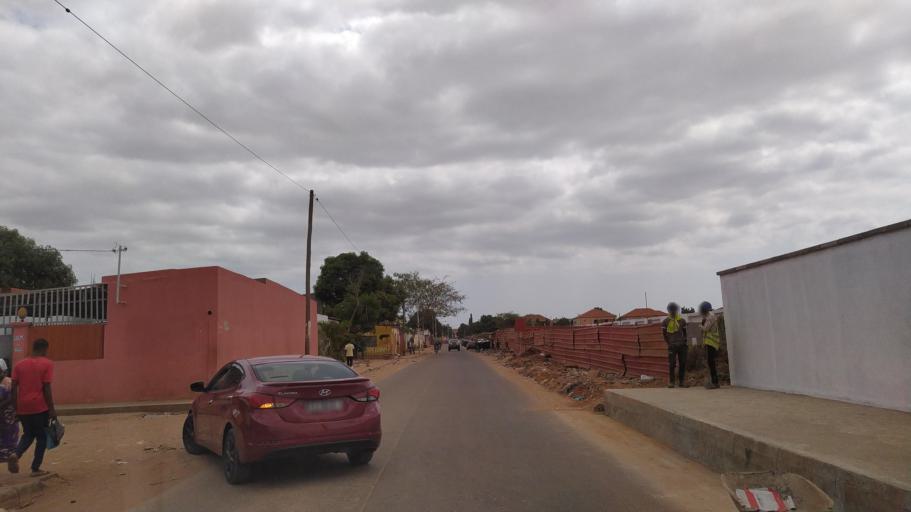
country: AO
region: Luanda
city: Luanda
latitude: -8.9316
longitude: 13.2588
